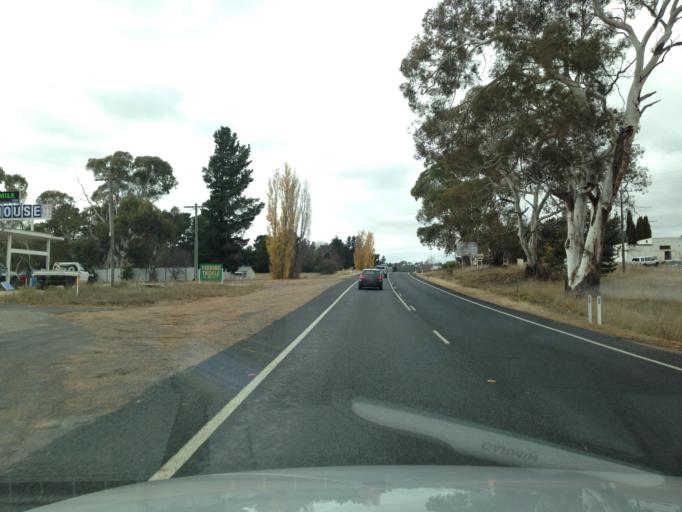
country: AU
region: New South Wales
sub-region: Cooma-Monaro
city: Cooma
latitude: -36.2455
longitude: 149.0546
